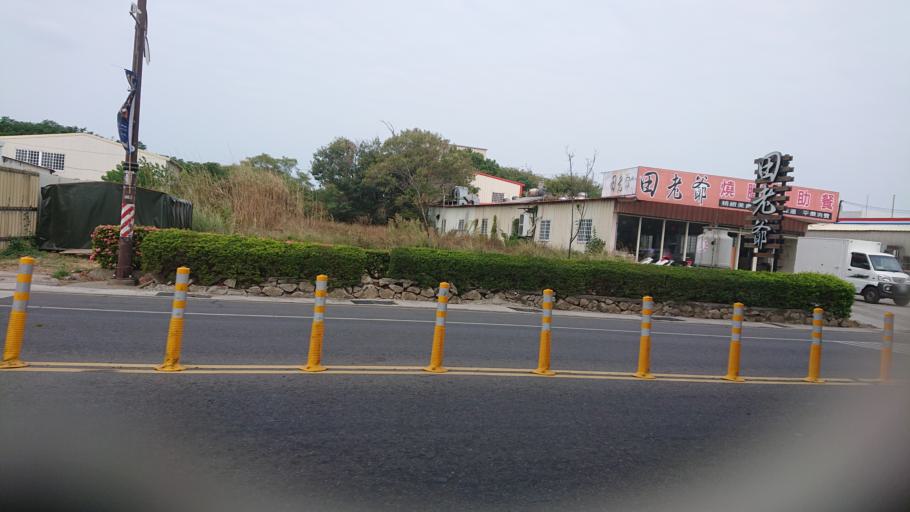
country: TW
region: Fukien
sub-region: Kinmen
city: Jincheng
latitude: 24.4353
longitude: 118.3273
